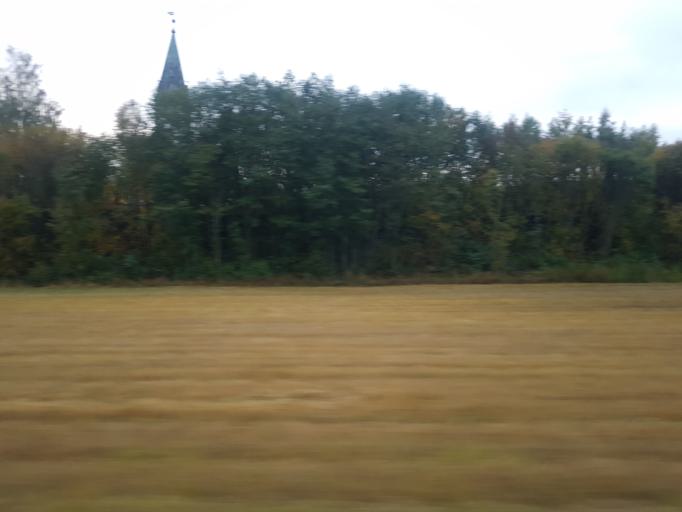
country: NO
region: Sor-Trondelag
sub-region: Melhus
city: Lundamo
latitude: 63.1301
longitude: 10.2510
